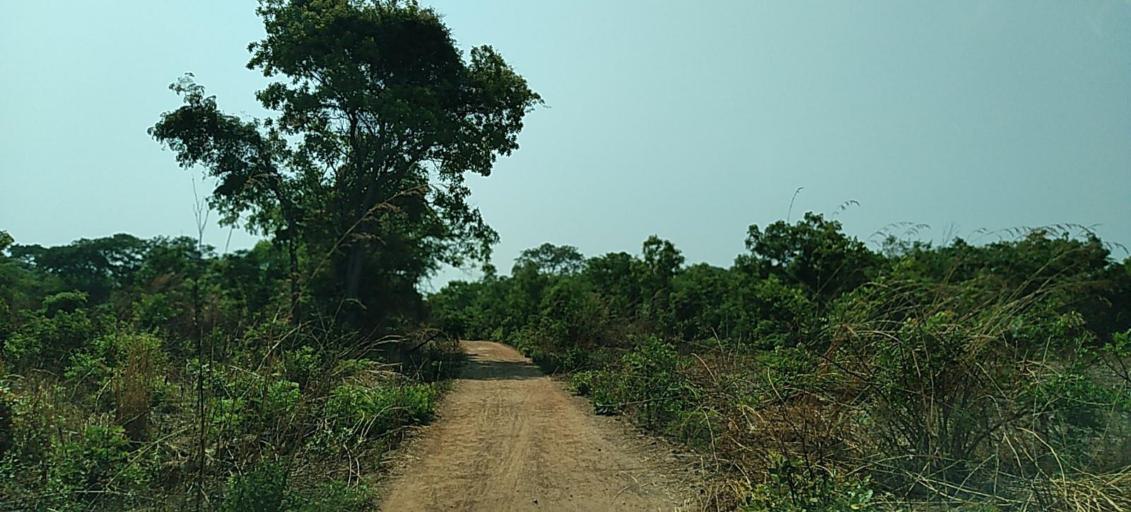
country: ZM
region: Copperbelt
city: Luanshya
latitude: -13.2775
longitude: 28.3067
